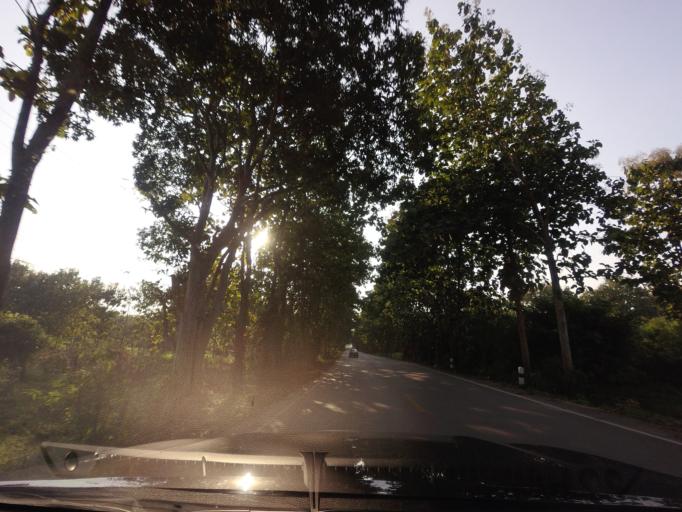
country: TH
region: Nan
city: Na Noi
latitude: 18.3346
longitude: 100.7591
